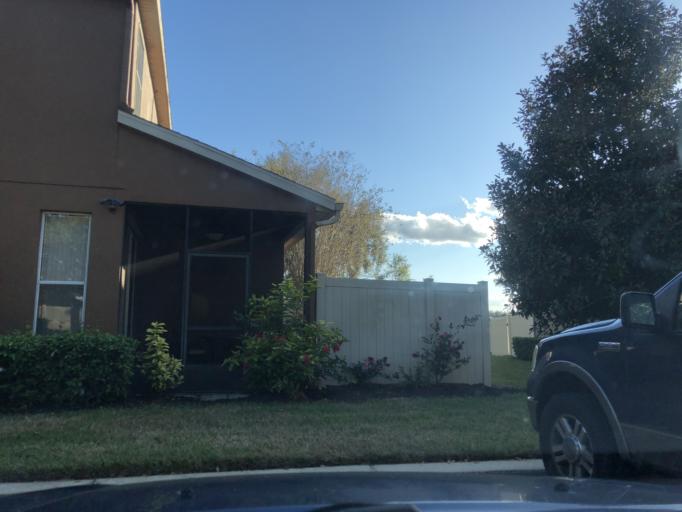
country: US
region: Florida
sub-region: Seminole County
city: Goldenrod
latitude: 28.6163
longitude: -81.2642
